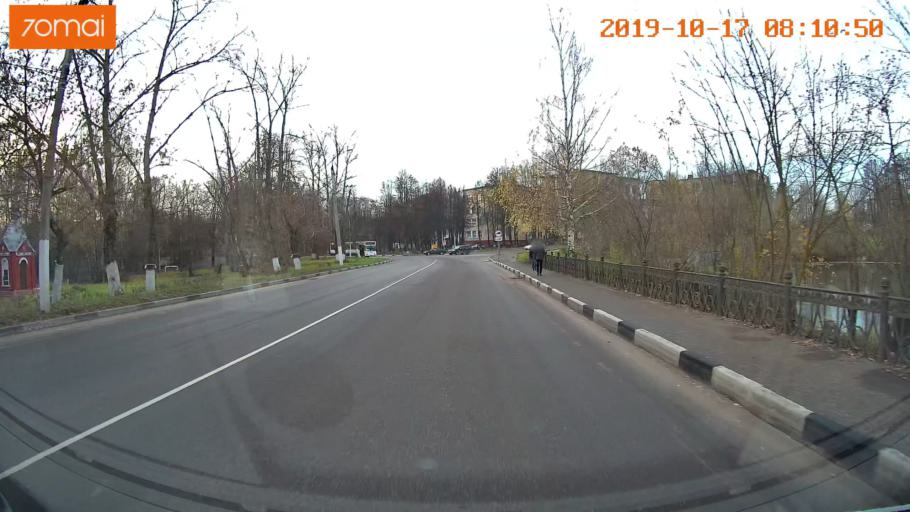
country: RU
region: Vladimir
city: Kol'chugino
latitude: 56.3054
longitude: 39.3770
